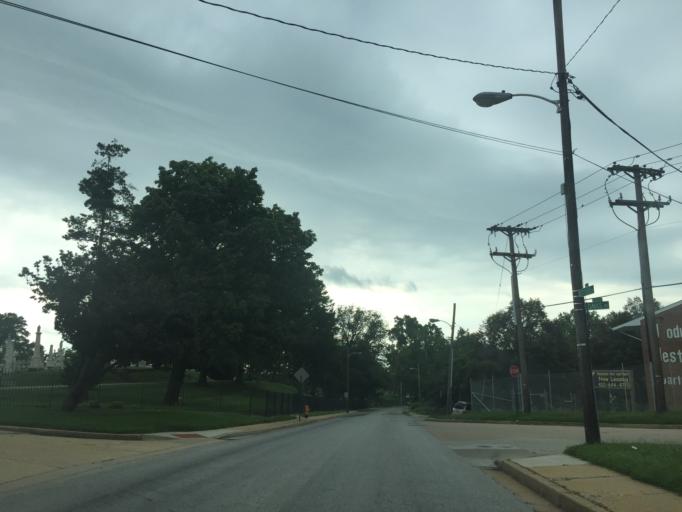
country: US
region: Maryland
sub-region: Baltimore County
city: Charlestown
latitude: 39.2874
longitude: -76.6874
